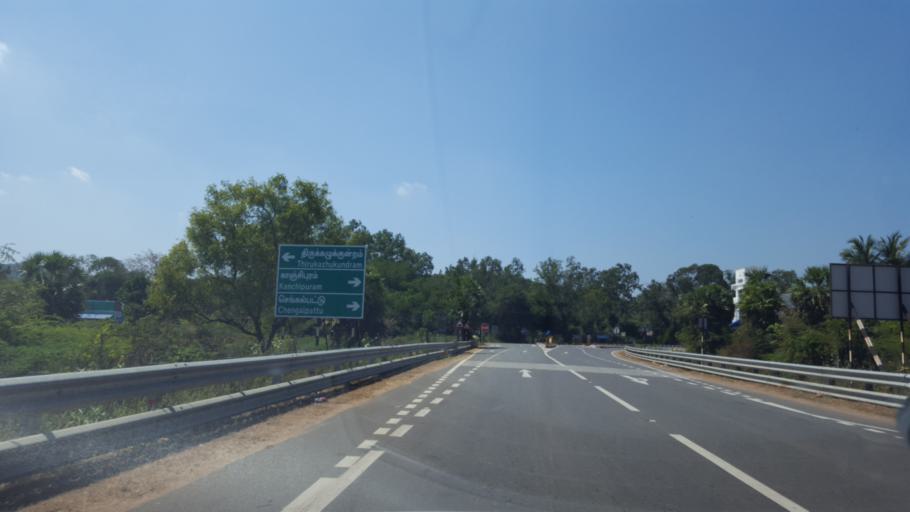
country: IN
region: Tamil Nadu
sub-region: Kancheepuram
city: Karumbakkam
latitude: 12.6247
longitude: 80.0536
